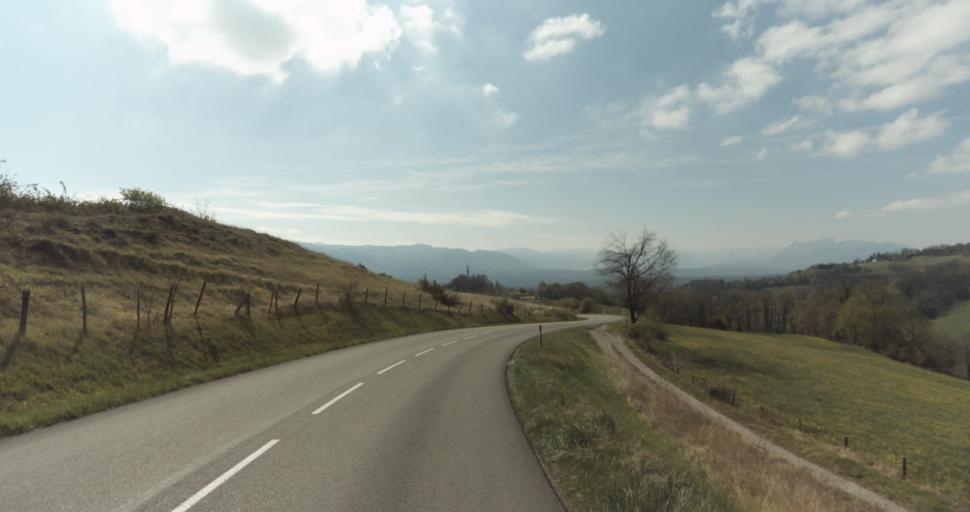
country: FR
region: Rhone-Alpes
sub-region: Departement de l'Isere
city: Saint-Verand
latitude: 45.1742
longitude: 5.3176
